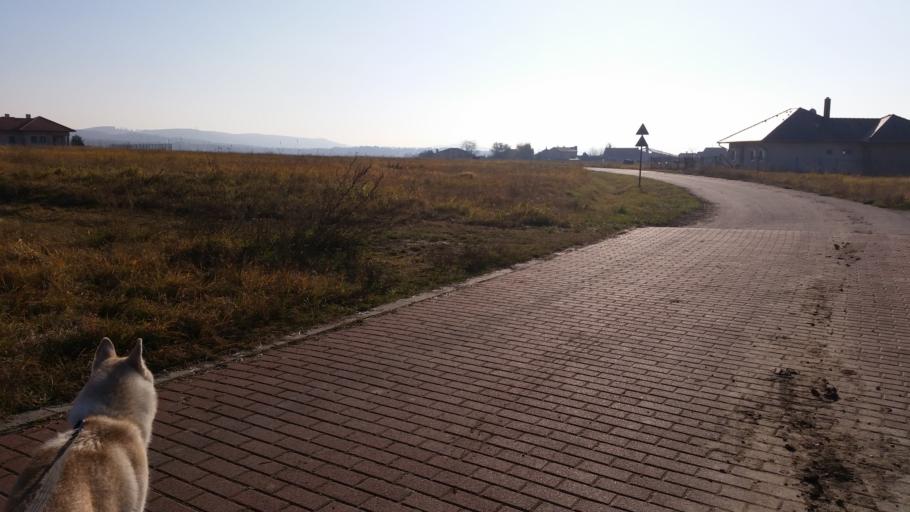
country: HU
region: Pest
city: Telki
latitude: 47.5628
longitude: 18.8080
